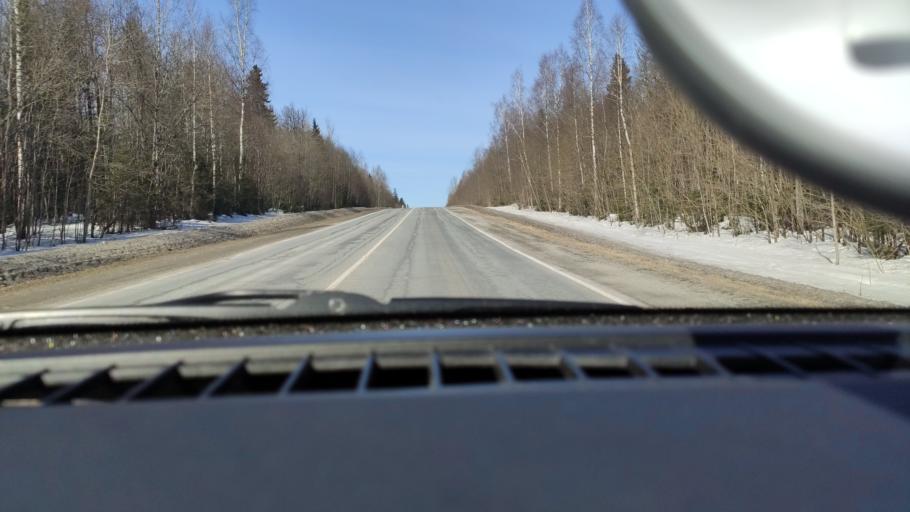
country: RU
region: Perm
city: Perm
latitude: 58.1776
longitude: 56.2280
